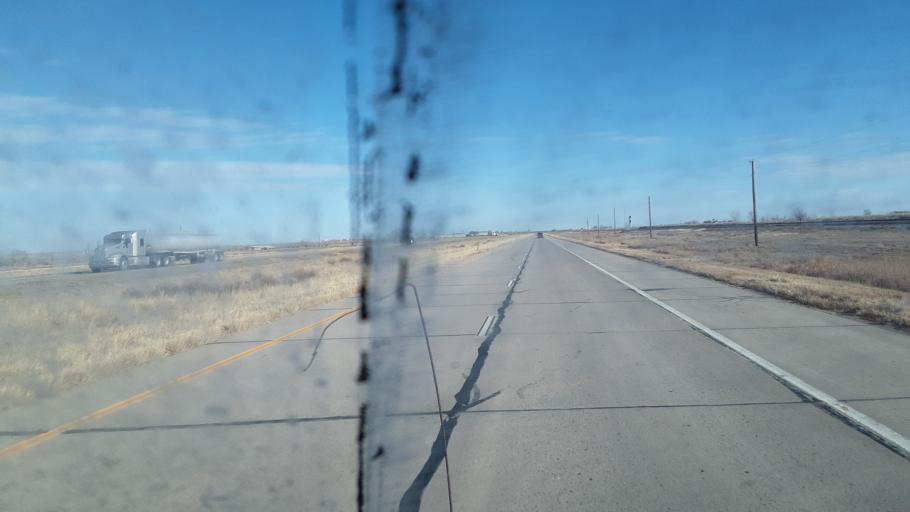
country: US
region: Colorado
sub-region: Morgan County
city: Fort Morgan
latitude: 40.2443
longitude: -103.9592
